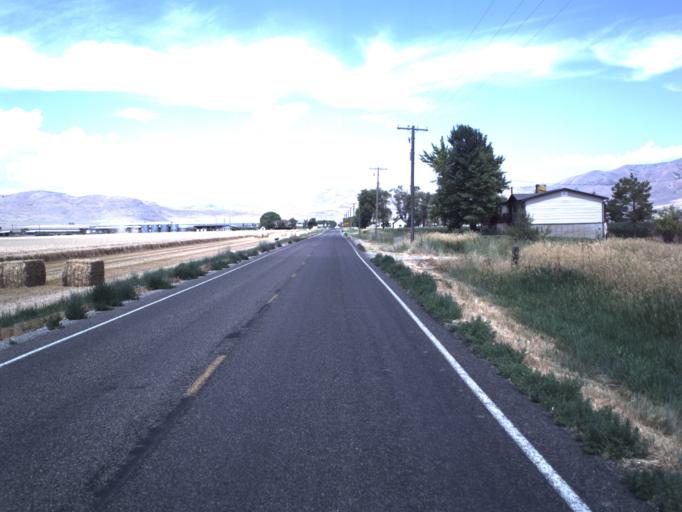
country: US
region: Utah
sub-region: Box Elder County
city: Tremonton
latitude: 41.7033
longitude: -112.2780
